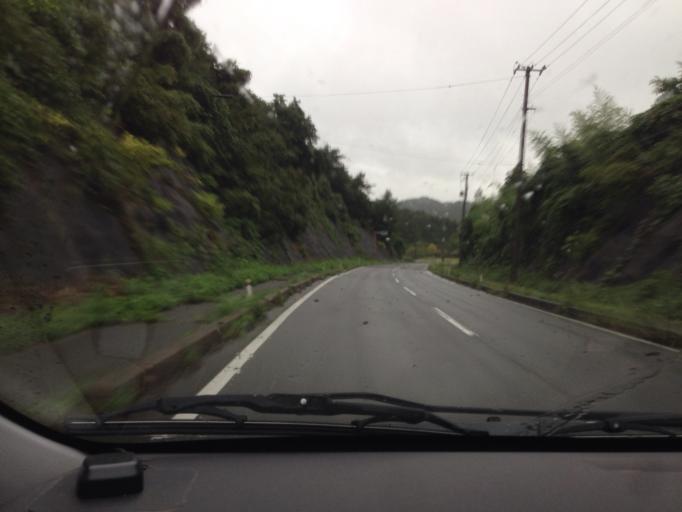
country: JP
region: Fukushima
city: Koriyama
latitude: 37.4120
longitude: 140.2700
